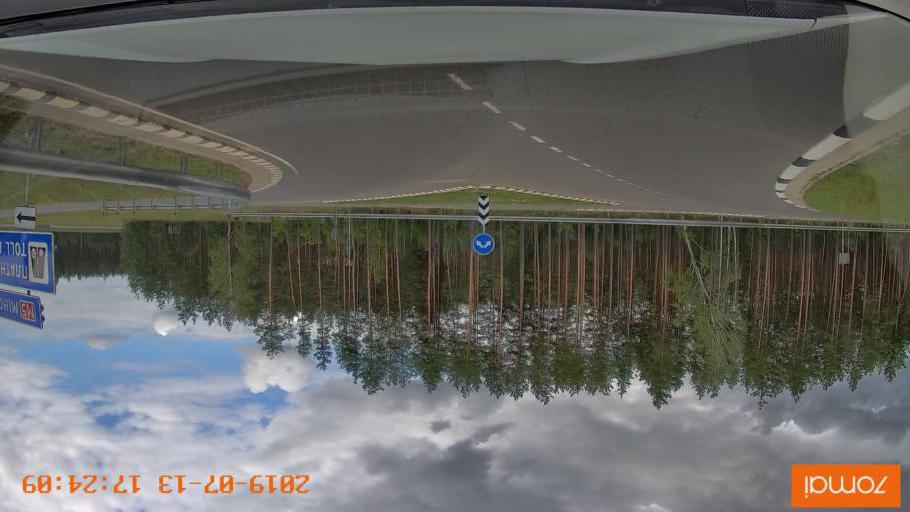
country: BY
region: Mogilev
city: Babruysk
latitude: 53.2540
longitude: 29.2381
